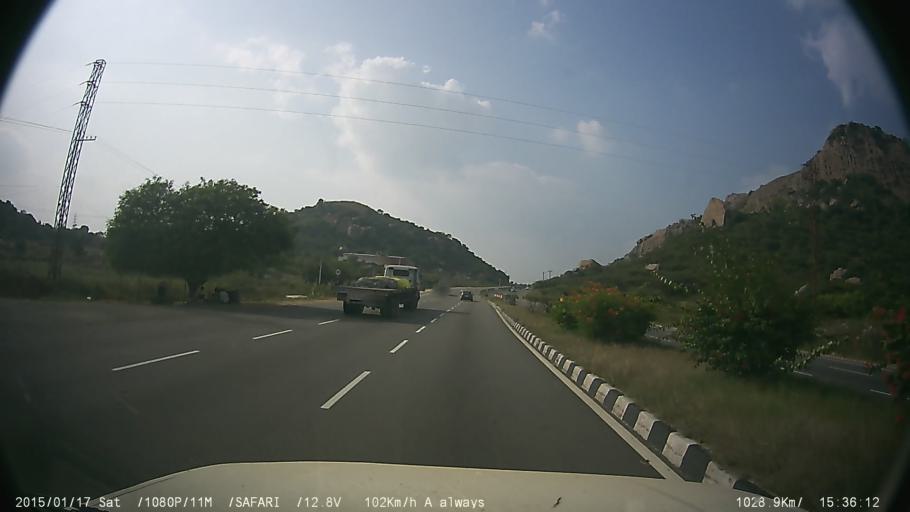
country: IN
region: Tamil Nadu
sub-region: Krishnagiri
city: Kelamangalam
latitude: 12.6548
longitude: 78.0249
